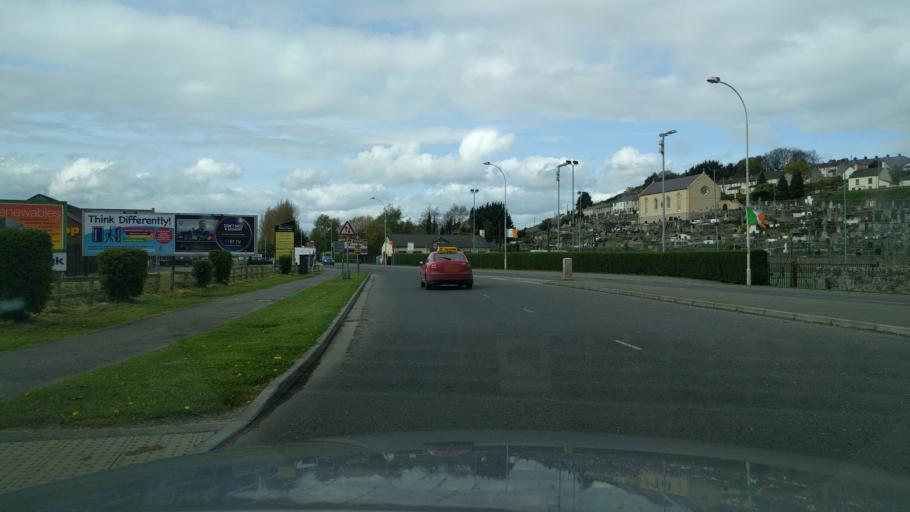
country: GB
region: Northern Ireland
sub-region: Newry and Mourne District
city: Newry
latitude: 54.1644
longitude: -6.3324
